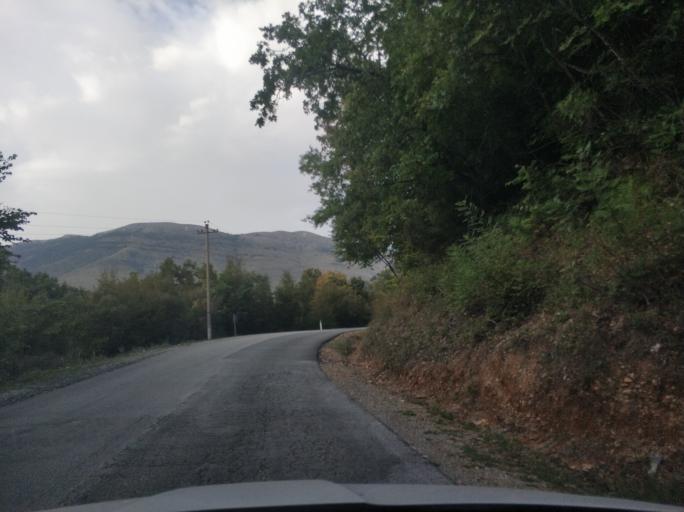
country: AL
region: Vlore
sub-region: Rrethi i Sarandes
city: Dhiver
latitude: 39.9203
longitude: 20.2011
